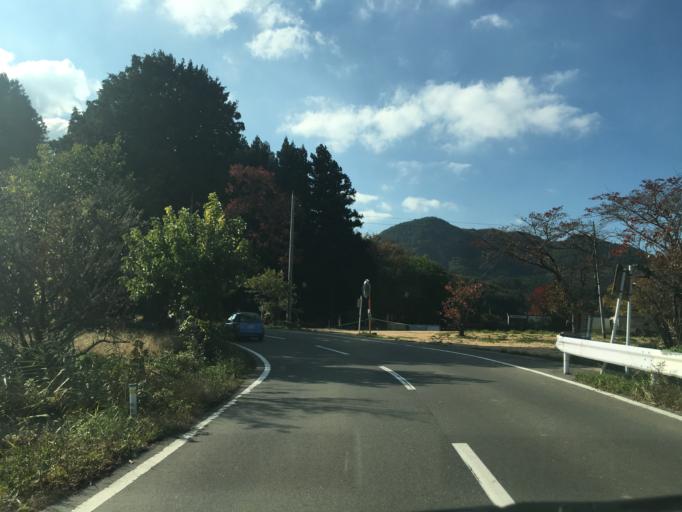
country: JP
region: Fukushima
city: Sukagawa
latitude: 37.2759
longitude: 140.1621
